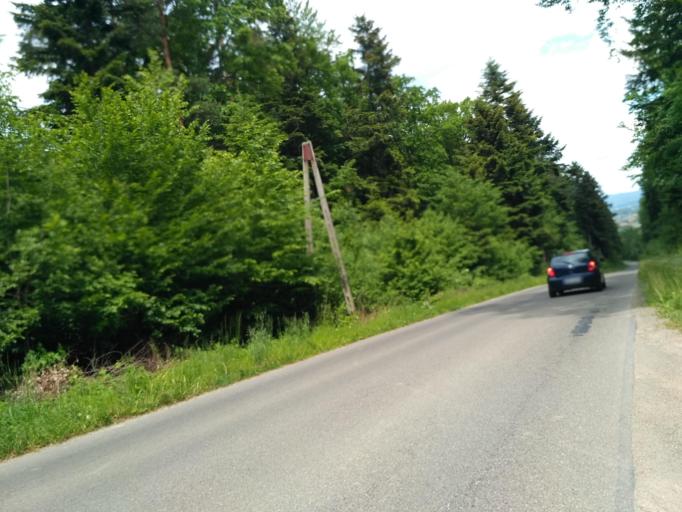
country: PL
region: Subcarpathian Voivodeship
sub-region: Powiat krosnienski
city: Chorkowka
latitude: 49.6368
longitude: 21.6612
